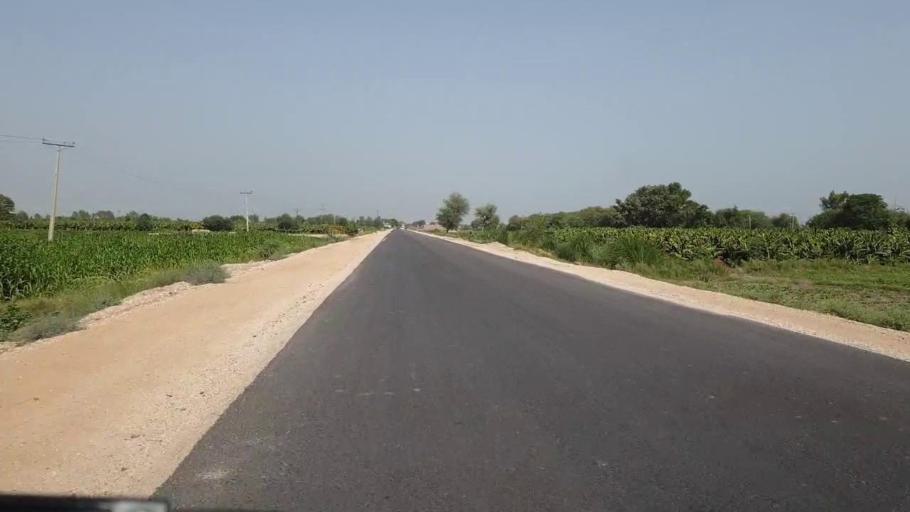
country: PK
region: Sindh
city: Sakrand
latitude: 26.2520
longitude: 68.2051
